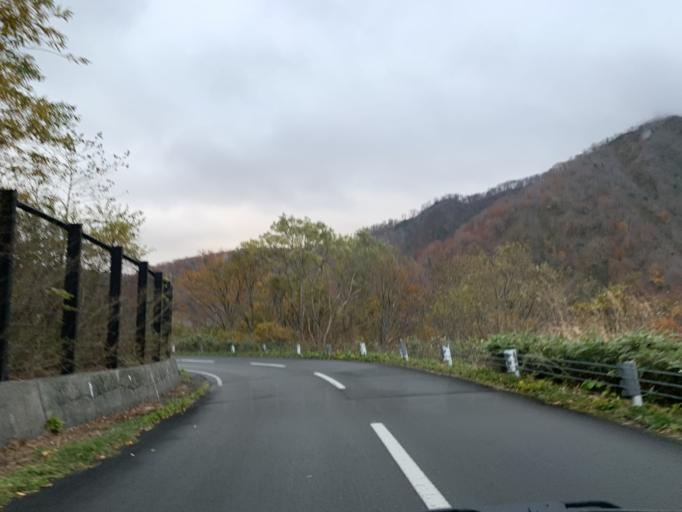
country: JP
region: Iwate
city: Mizusawa
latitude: 39.1166
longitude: 140.8343
